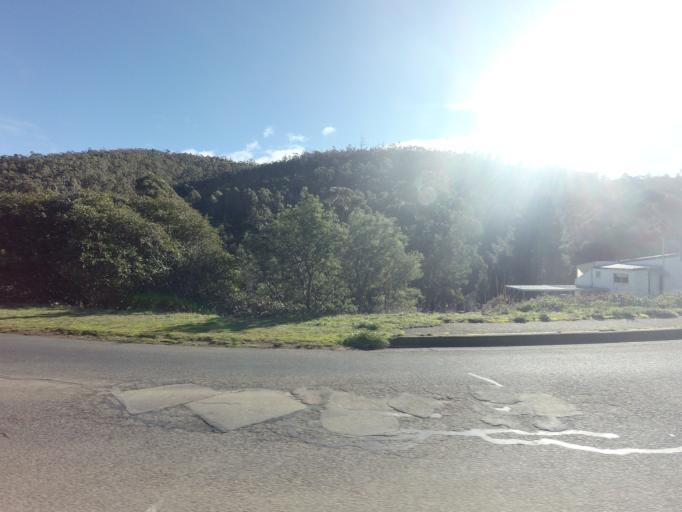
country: AU
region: Tasmania
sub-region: Glenorchy
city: Berriedale
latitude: -42.8178
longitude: 147.2231
